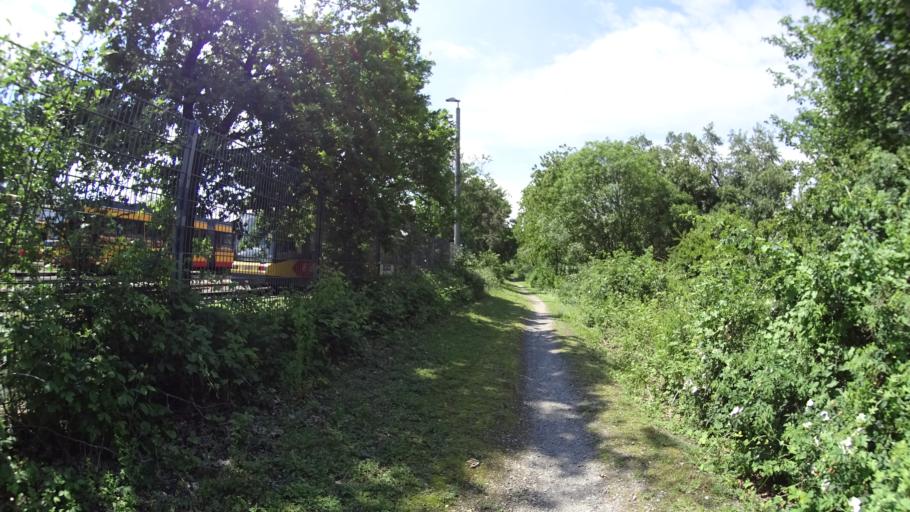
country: DE
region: Baden-Wuerttemberg
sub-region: Karlsruhe Region
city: Rheinstetten
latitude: 49.0246
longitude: 8.3362
